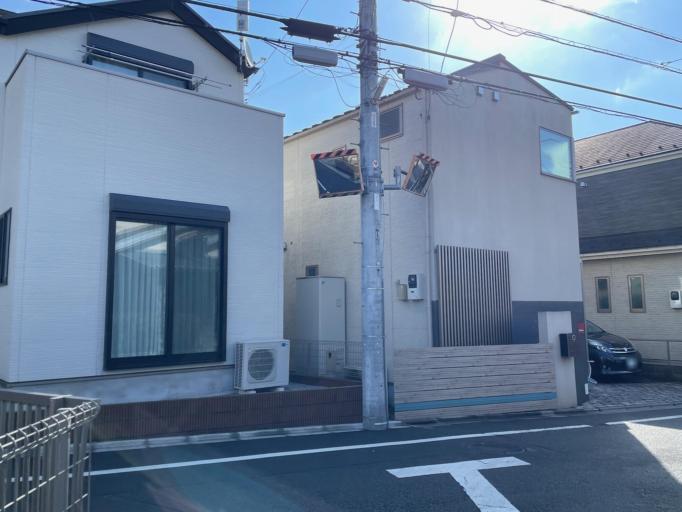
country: JP
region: Tokyo
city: Kokubunji
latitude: 35.6756
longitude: 139.4645
